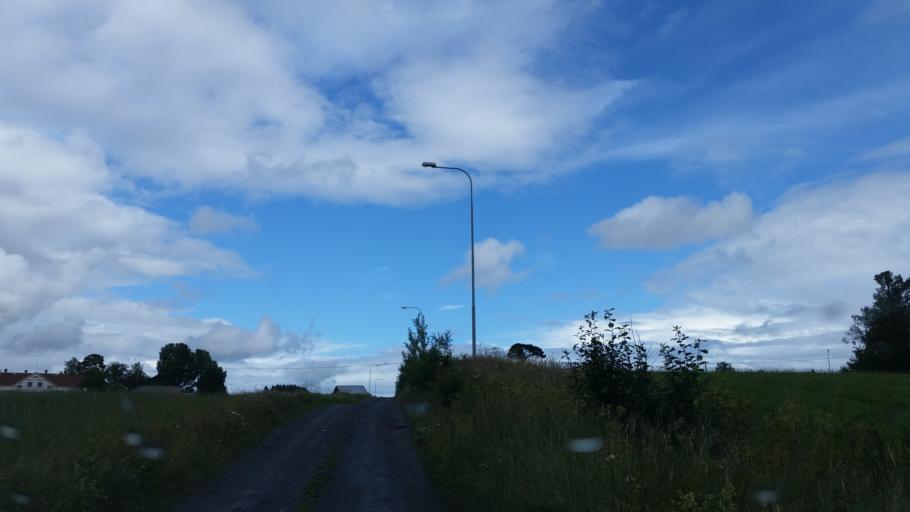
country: SE
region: Jaemtland
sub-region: Krokoms Kommun
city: Krokom
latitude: 63.3044
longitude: 14.3144
